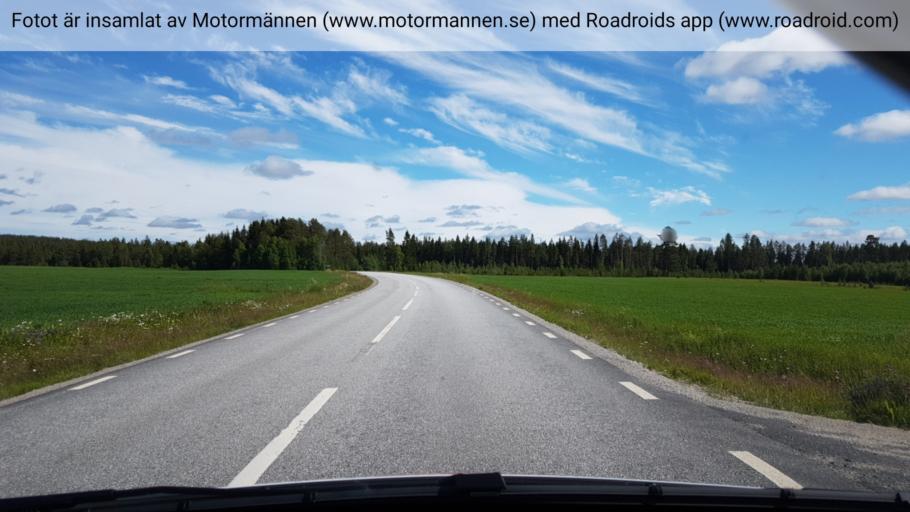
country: SE
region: Vaesterbotten
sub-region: Vindelns Kommun
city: Vindeln
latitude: 64.1058
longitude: 19.5924
